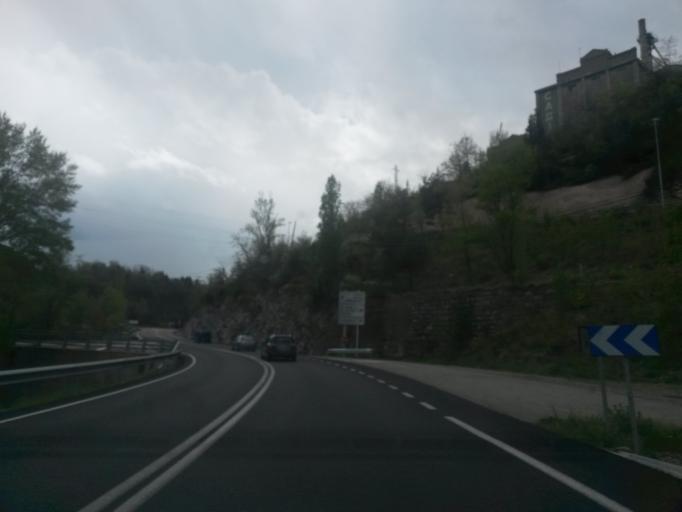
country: ES
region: Catalonia
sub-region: Provincia de Barcelona
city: Vallcebre
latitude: 42.1771
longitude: 1.8611
